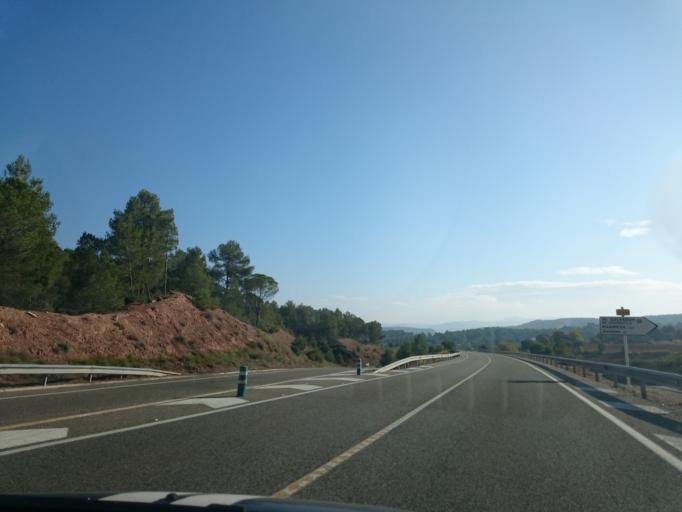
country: ES
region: Catalonia
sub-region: Provincia de Barcelona
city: Sant Salvador de Guardiola
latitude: 41.6894
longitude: 1.7706
